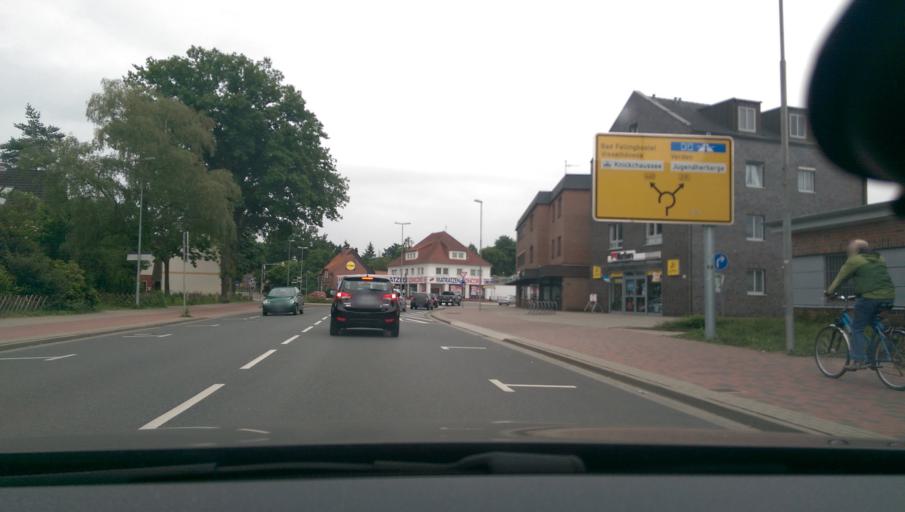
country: DE
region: Lower Saxony
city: Rotenburg
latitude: 53.1043
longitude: 9.3973
